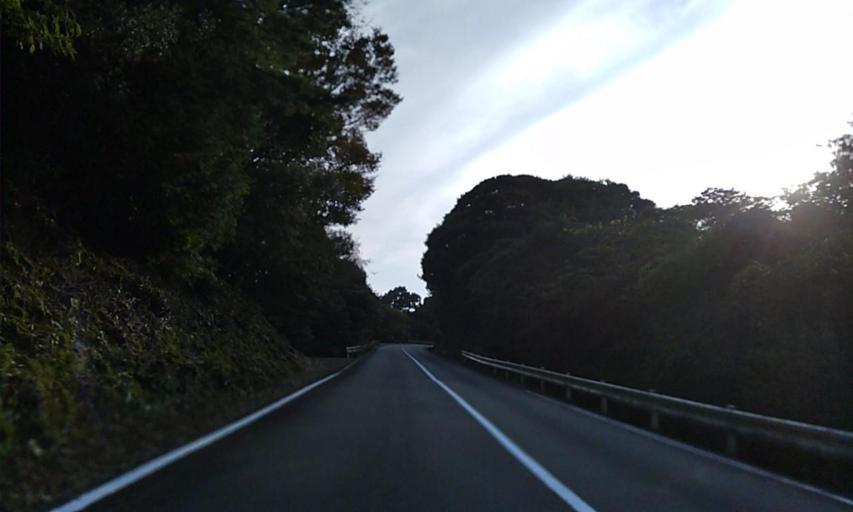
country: JP
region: Mie
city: Toba
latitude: 34.4713
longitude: 136.8287
